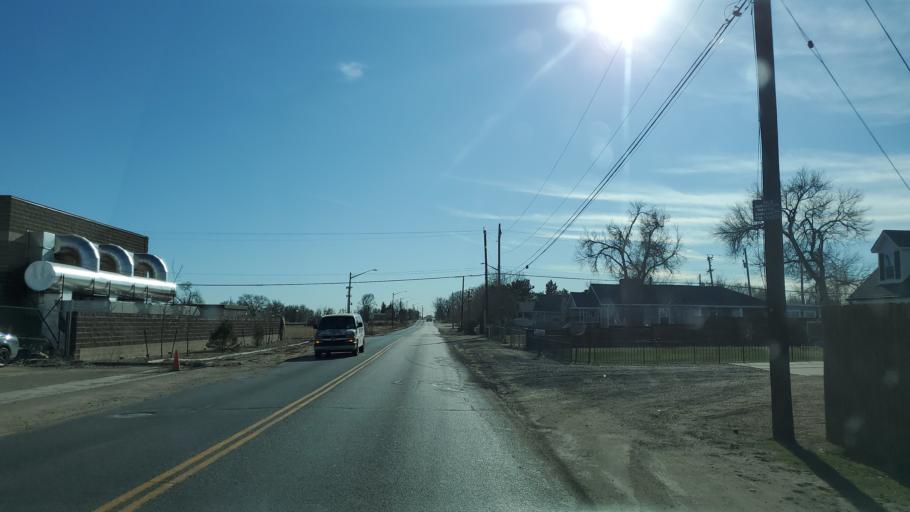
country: US
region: Colorado
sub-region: Adams County
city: Derby
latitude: 39.8497
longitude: -104.8996
